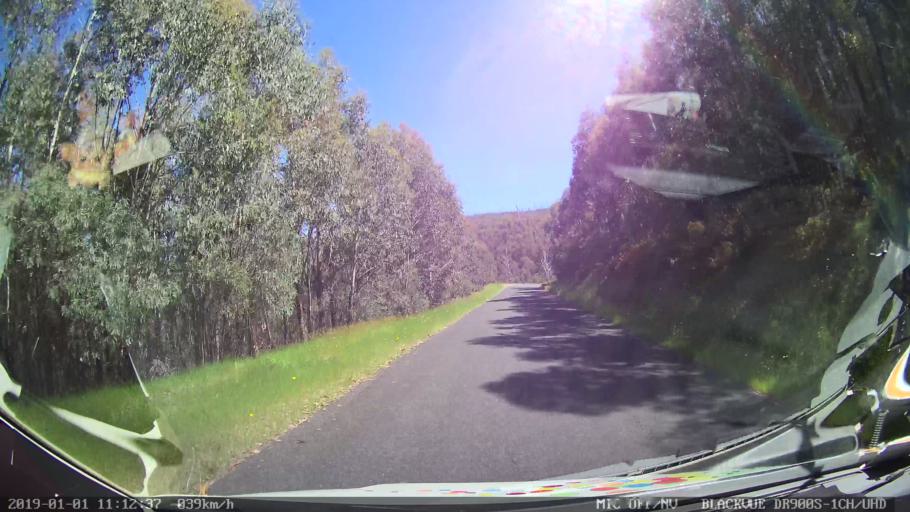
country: AU
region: New South Wales
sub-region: Snowy River
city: Jindabyne
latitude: -35.9561
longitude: 148.3992
